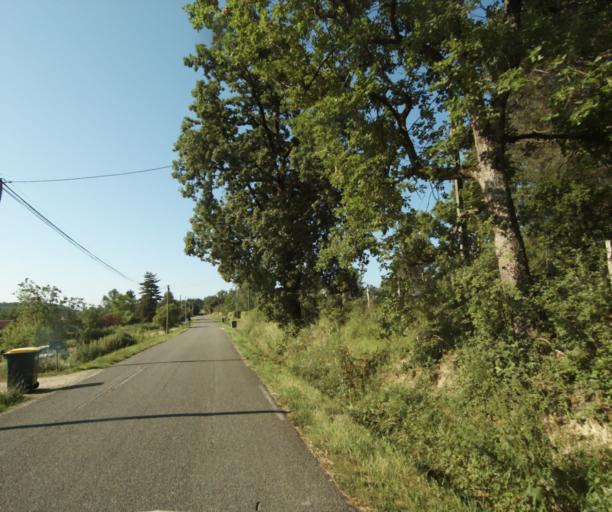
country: FR
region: Midi-Pyrenees
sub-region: Departement du Tarn-et-Garonne
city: Saint-Etienne-de-Tulmont
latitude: 44.0166
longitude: 1.4307
